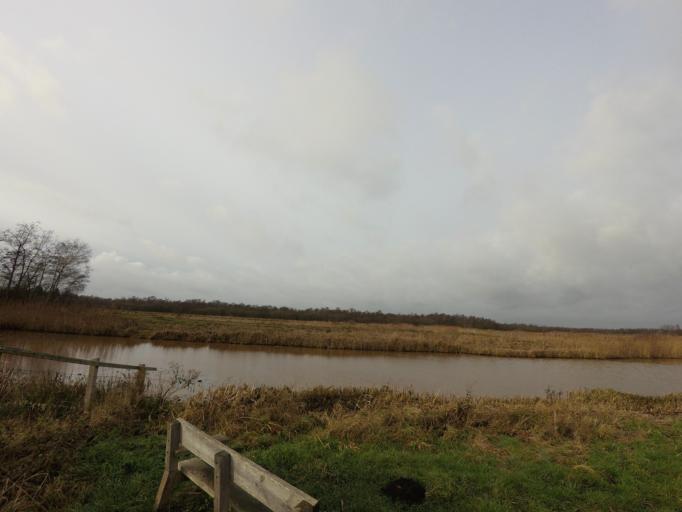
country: NL
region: North Holland
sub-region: Gemeente Wijdemeren
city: Nieuw-Loosdrecht
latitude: 52.1611
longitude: 5.1203
